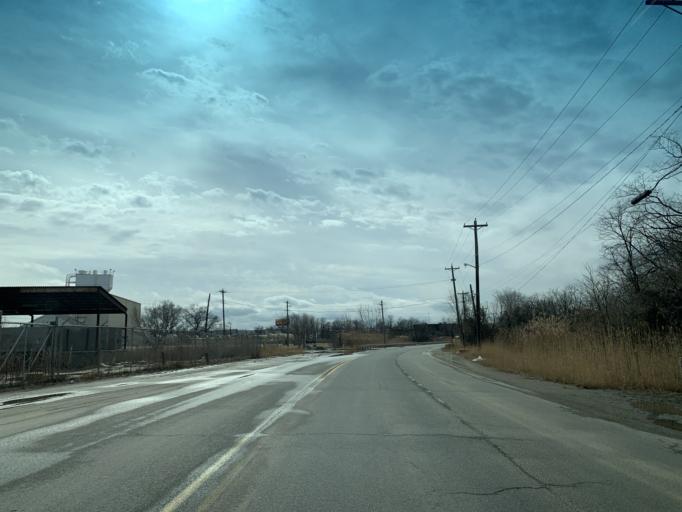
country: US
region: Delaware
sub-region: New Castle County
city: Wilmington
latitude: 39.7205
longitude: -75.5499
